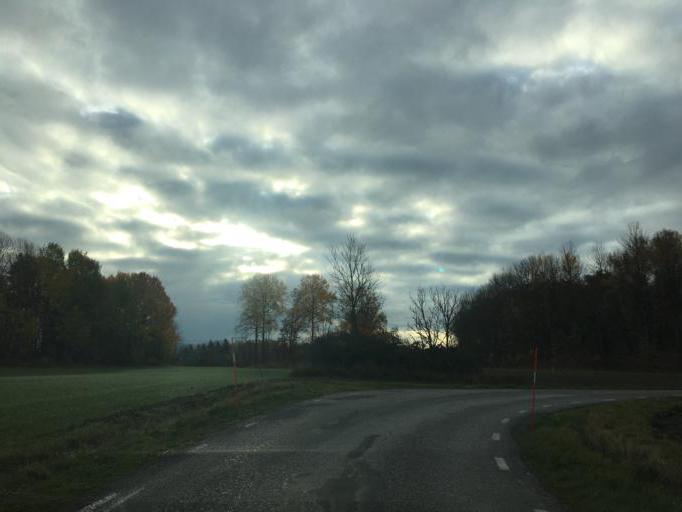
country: SE
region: Vaestmanland
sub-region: Vasteras
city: Vasteras
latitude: 59.5697
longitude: 16.4541
